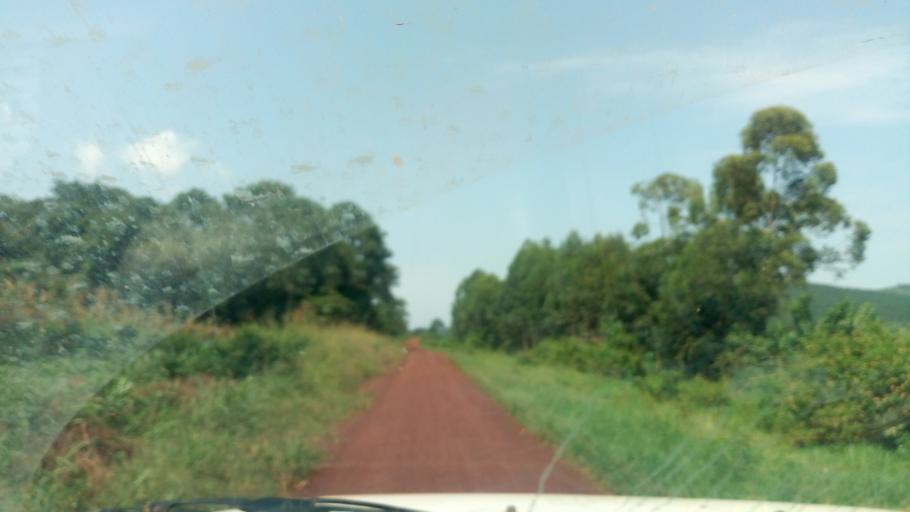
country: UG
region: Western Region
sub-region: Masindi District
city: Masindi
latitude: 1.6525
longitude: 31.8074
